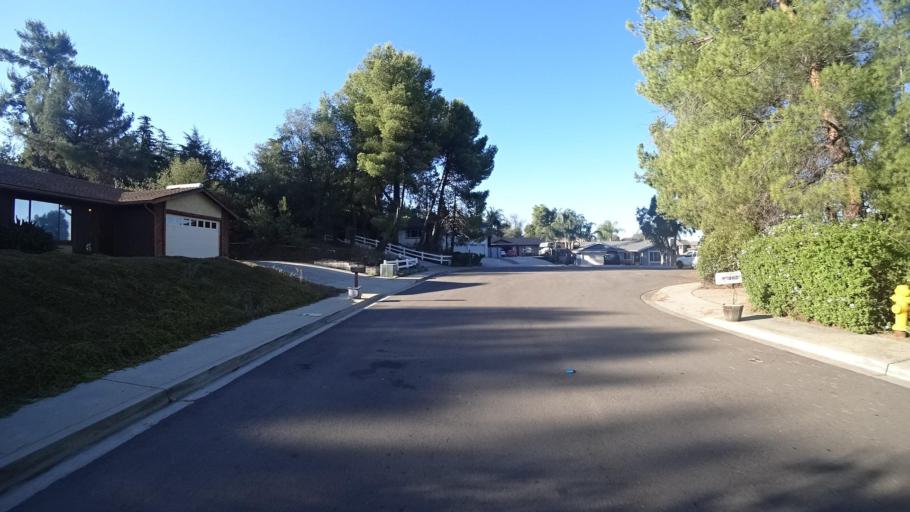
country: US
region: California
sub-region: San Diego County
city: Alpine
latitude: 32.8346
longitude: -116.7737
